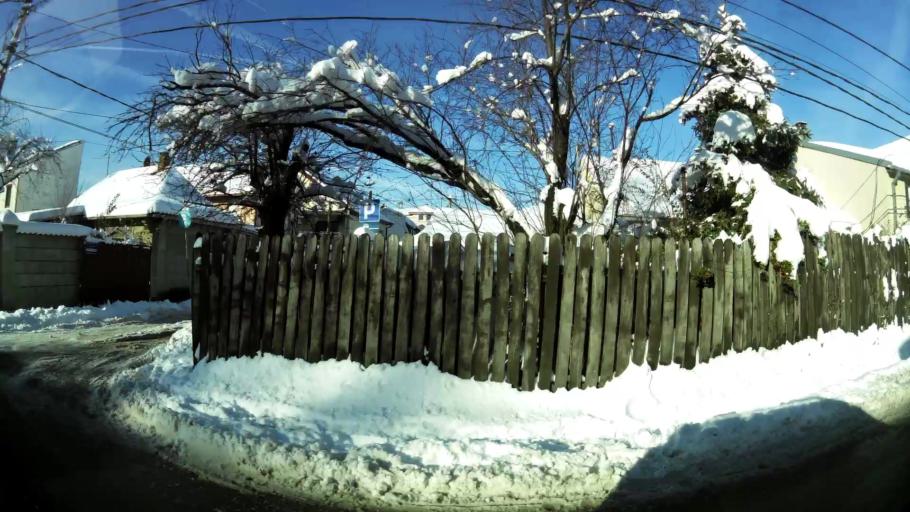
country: RS
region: Central Serbia
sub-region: Belgrade
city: Vracar
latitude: 44.7900
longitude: 20.4891
